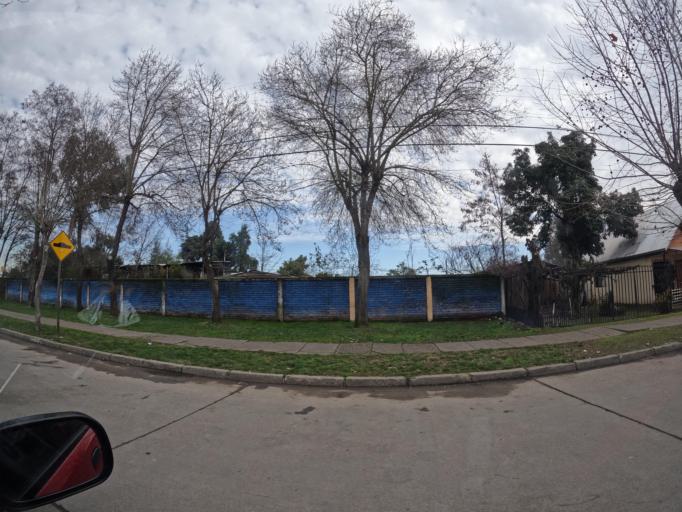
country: CL
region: Maule
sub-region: Provincia de Linares
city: Linares
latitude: -35.8556
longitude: -71.5858
